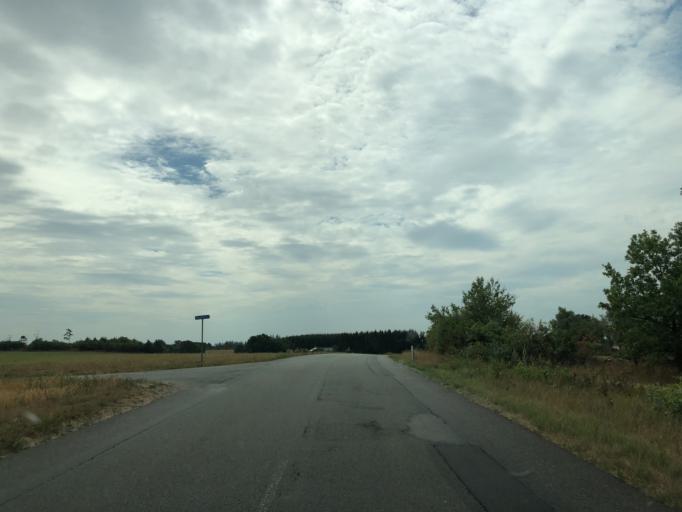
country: DK
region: South Denmark
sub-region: Vejle Kommune
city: Egtved
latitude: 55.6215
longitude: 9.1932
